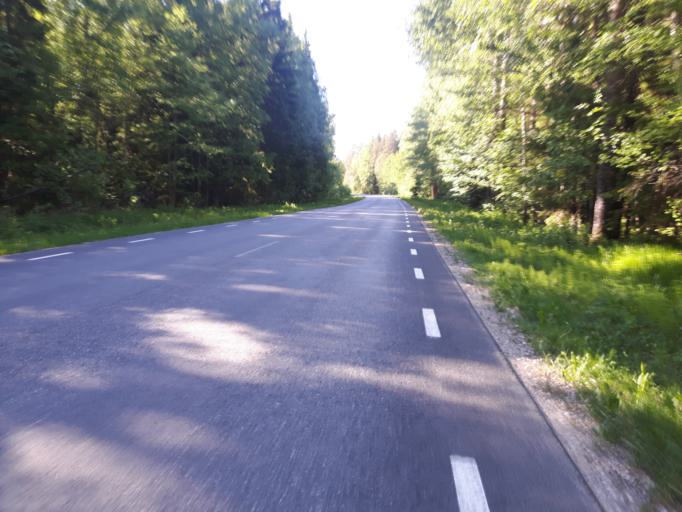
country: EE
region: Laeaene-Virumaa
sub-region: Kadrina vald
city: Kadrina
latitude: 59.5468
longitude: 26.0200
